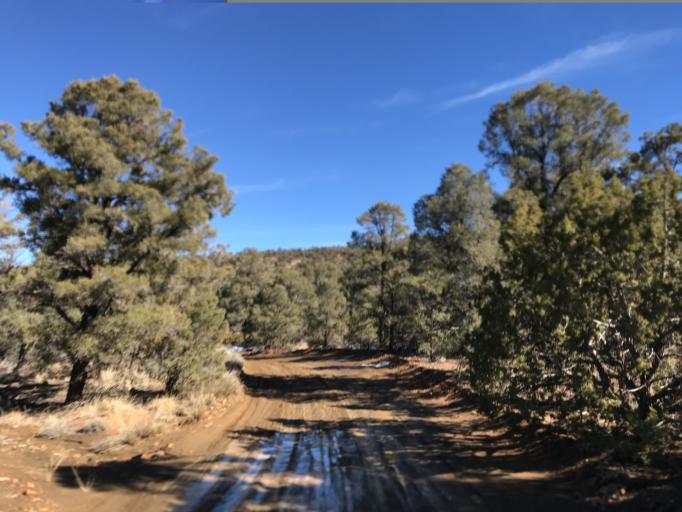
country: US
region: California
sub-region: San Bernardino County
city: Big Bear City
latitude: 34.2511
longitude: -116.7247
